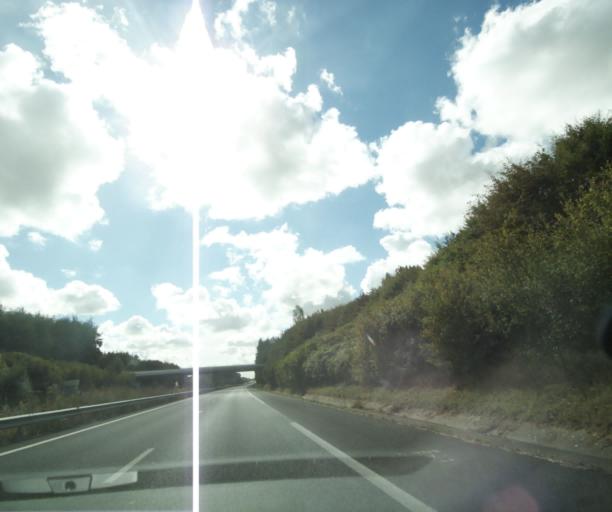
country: FR
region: Poitou-Charentes
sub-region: Departement de la Charente-Maritime
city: Cabariot
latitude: 45.9374
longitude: -0.8429
